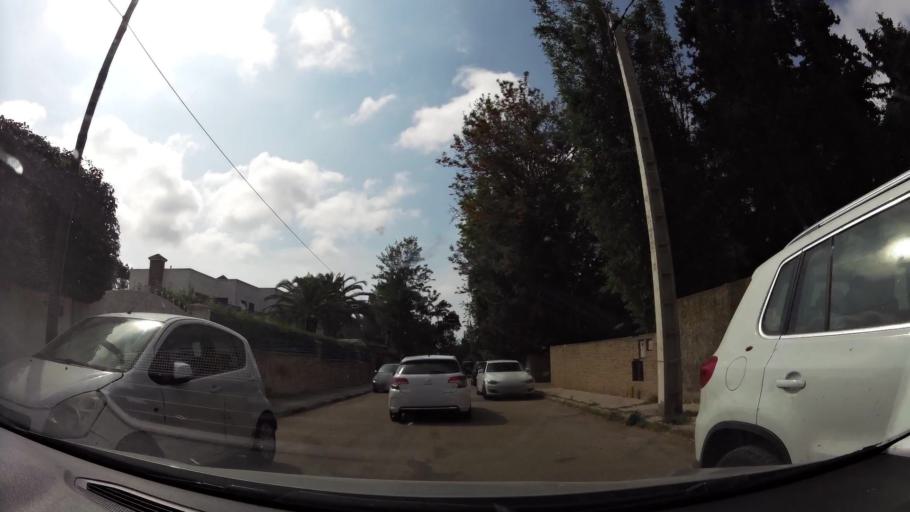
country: MA
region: Rabat-Sale-Zemmour-Zaer
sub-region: Rabat
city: Rabat
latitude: 33.9733
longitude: -6.8467
